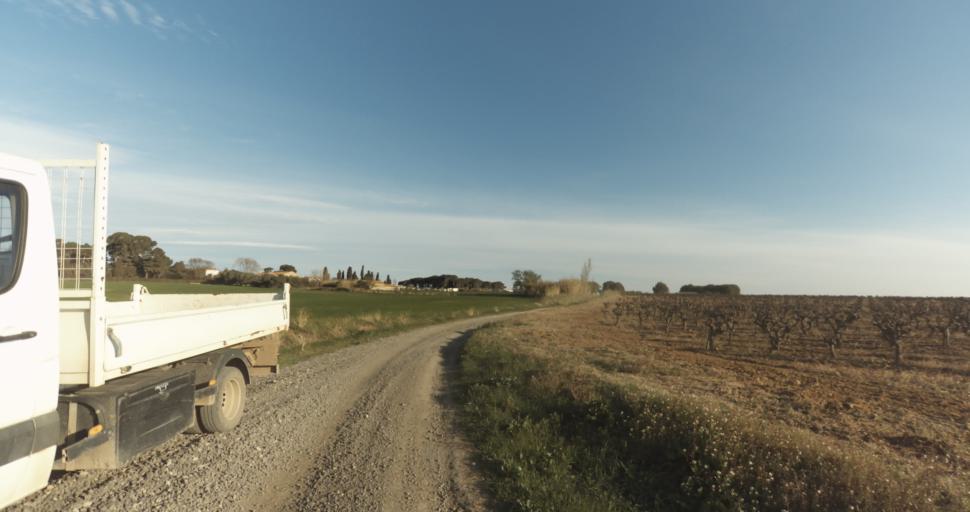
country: FR
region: Languedoc-Roussillon
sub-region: Departement de l'Herault
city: Pomerols
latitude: 43.3805
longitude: 3.5211
